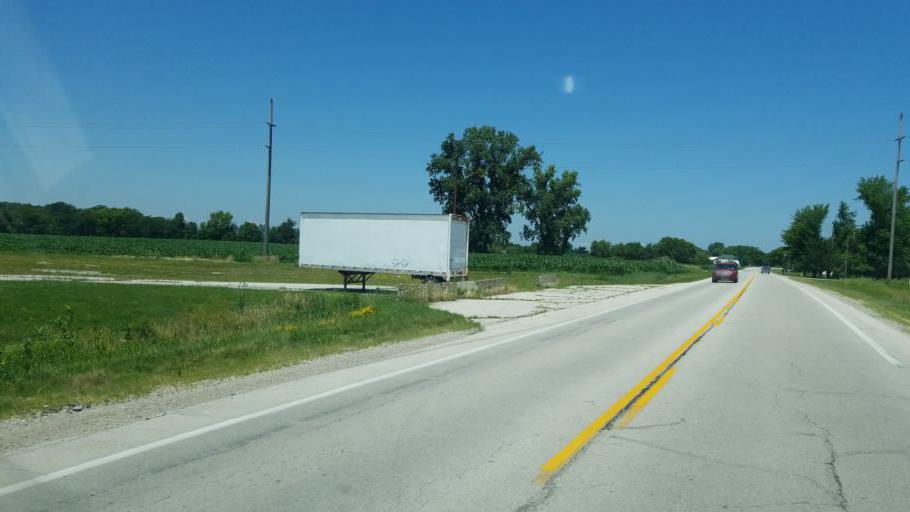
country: US
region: Ohio
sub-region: Sandusky County
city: Fremont
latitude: 41.4069
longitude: -83.1001
